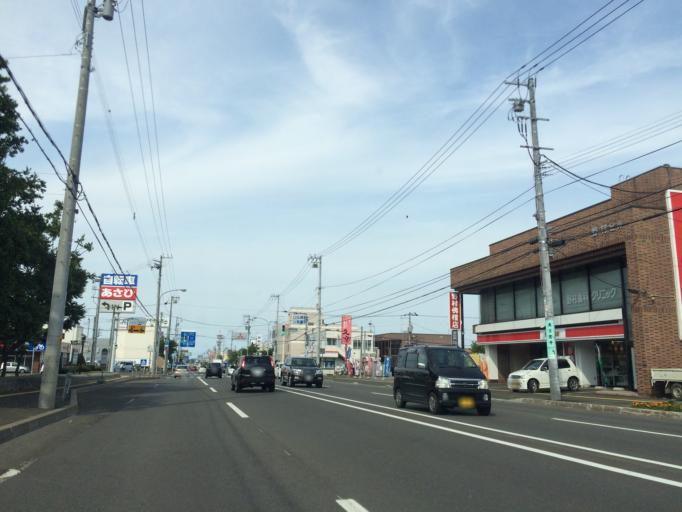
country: JP
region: Hokkaido
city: Ebetsu
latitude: 43.1029
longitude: 141.5376
